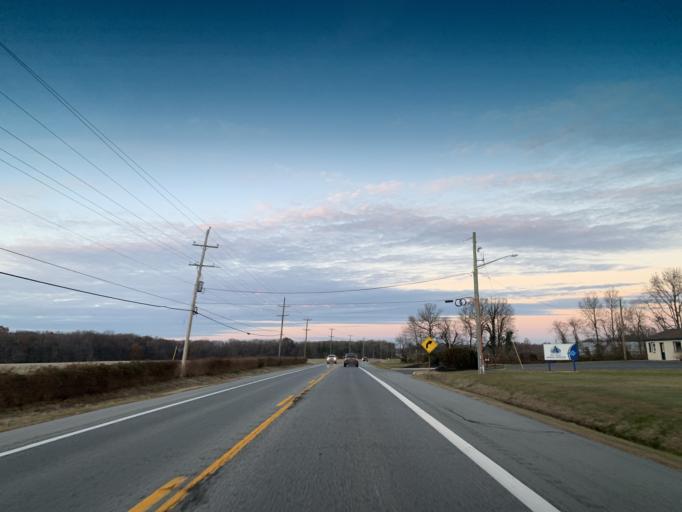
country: US
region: Maryland
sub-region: Cecil County
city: Elkton
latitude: 39.4932
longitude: -75.8427
